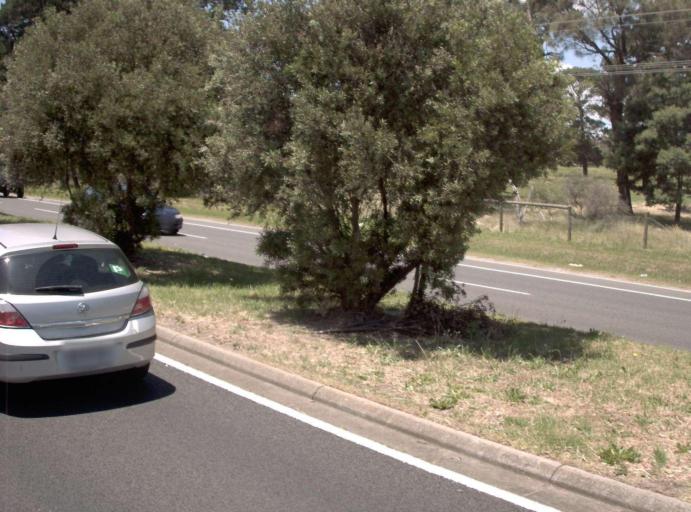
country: AU
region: Victoria
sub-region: Mornington Peninsula
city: Mount Eliza
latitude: -38.2059
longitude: 145.0751
